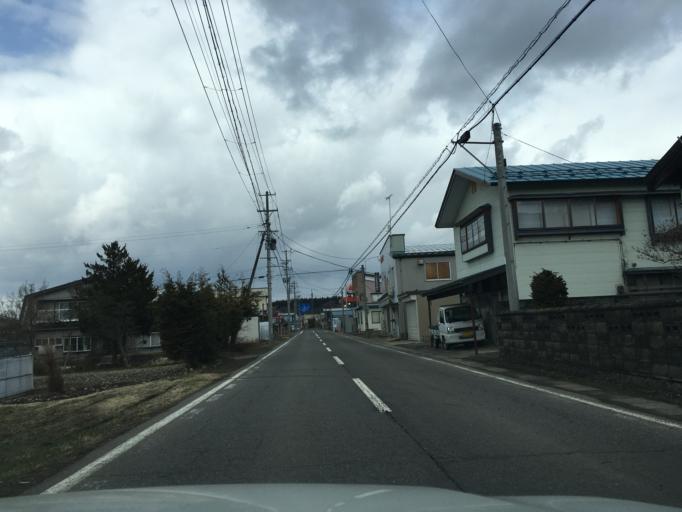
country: JP
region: Akita
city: Takanosu
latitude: 40.1564
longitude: 140.3344
